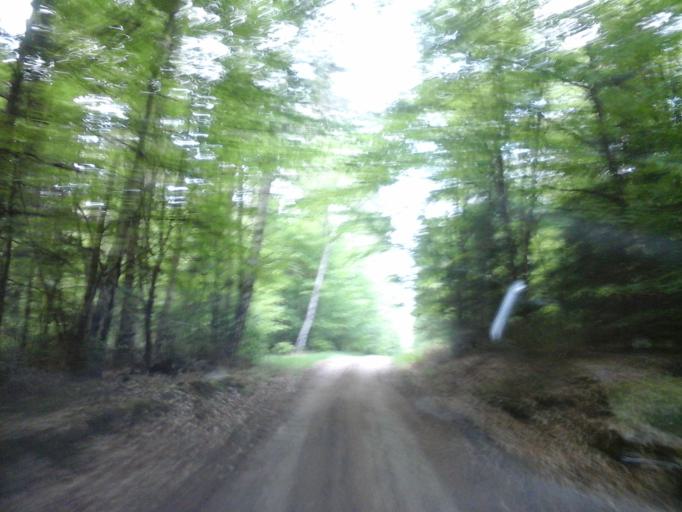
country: PL
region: West Pomeranian Voivodeship
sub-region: Powiat choszczenski
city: Pelczyce
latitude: 52.9506
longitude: 15.3538
